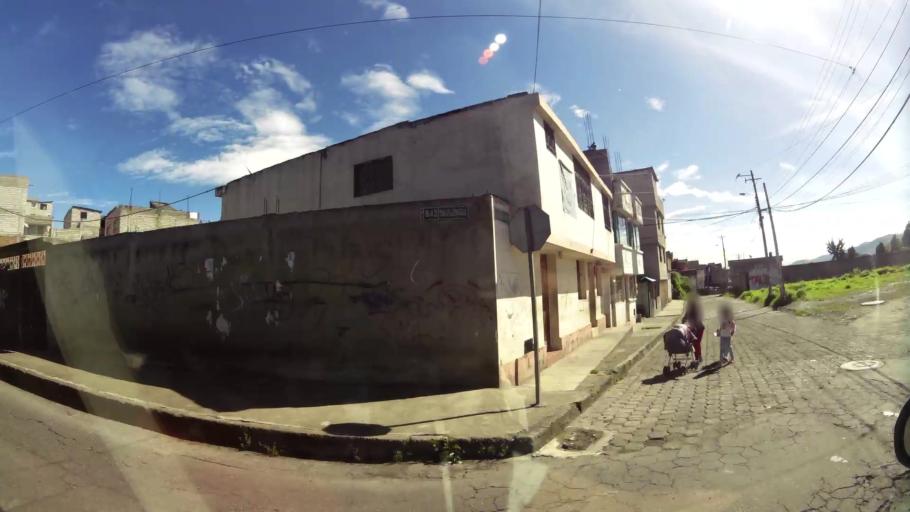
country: EC
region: Pichincha
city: Quito
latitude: -0.3041
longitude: -78.5618
